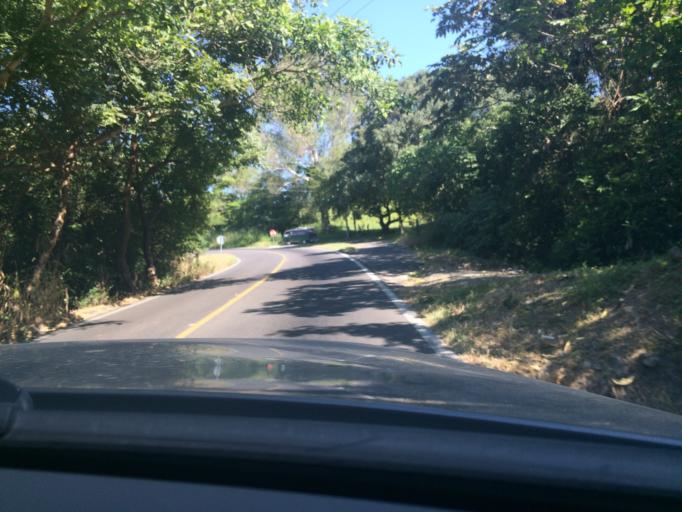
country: MX
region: Colima
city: Suchitlan
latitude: 19.3697
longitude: -103.7221
